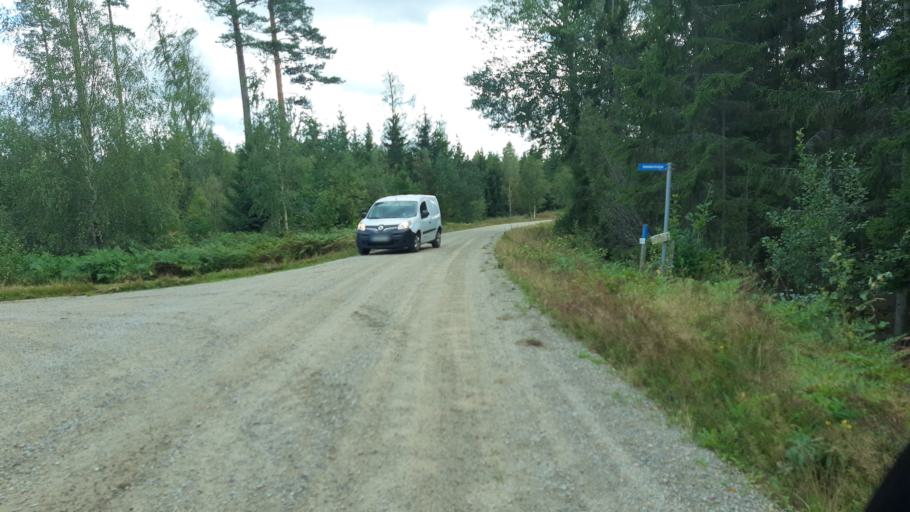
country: SE
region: Blekinge
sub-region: Ronneby Kommun
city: Brakne-Hoby
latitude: 56.4314
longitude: 15.1850
